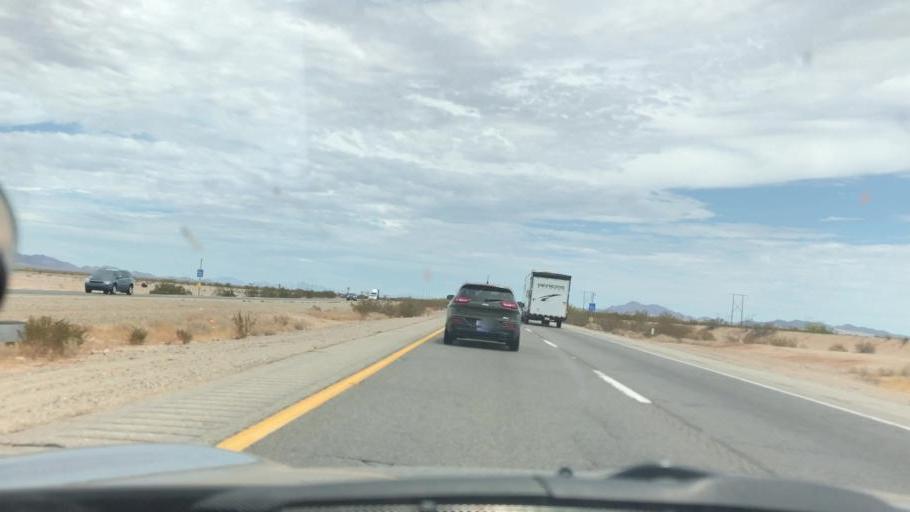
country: US
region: California
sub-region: Riverside County
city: Mesa Verde
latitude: 33.6074
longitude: -114.9898
